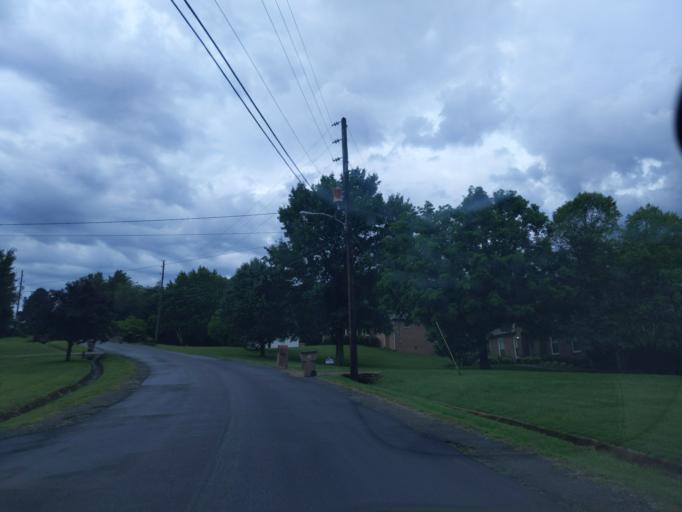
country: US
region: Tennessee
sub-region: Williamson County
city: Brentwood Estates
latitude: 36.0389
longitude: -86.7399
